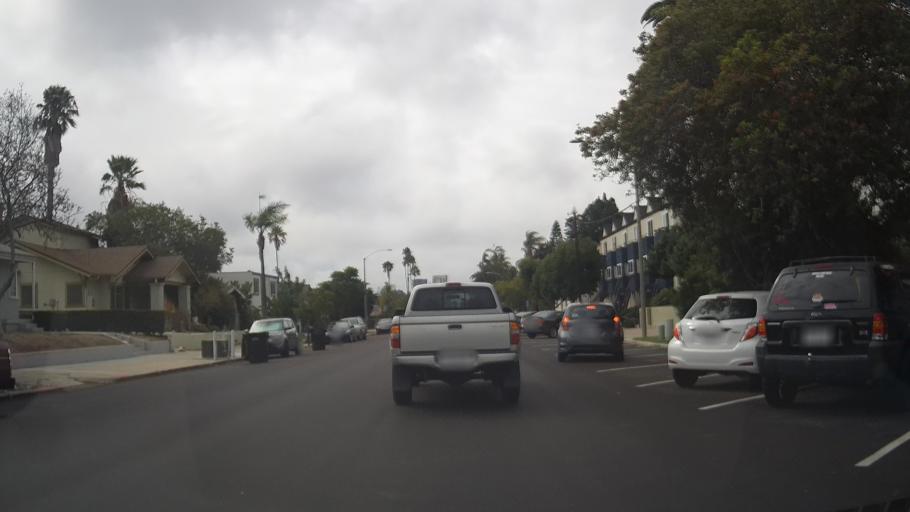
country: US
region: California
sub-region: San Diego County
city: San Diego
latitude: 32.7190
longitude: -117.1363
